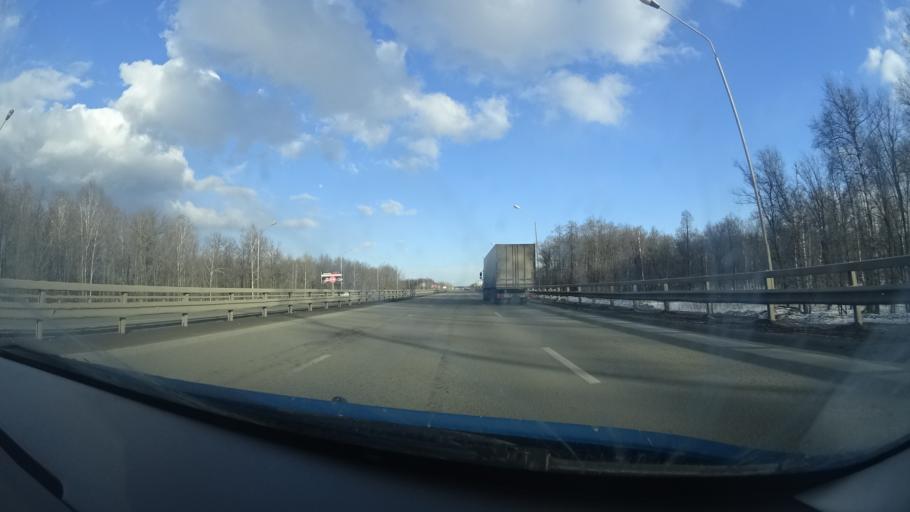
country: RU
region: Bashkortostan
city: Avdon
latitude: 54.6688
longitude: 55.8444
